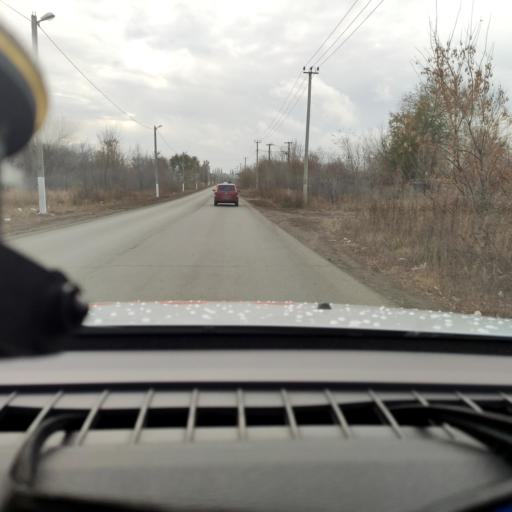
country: RU
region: Samara
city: Chapayevsk
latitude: 52.9919
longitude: 49.7301
